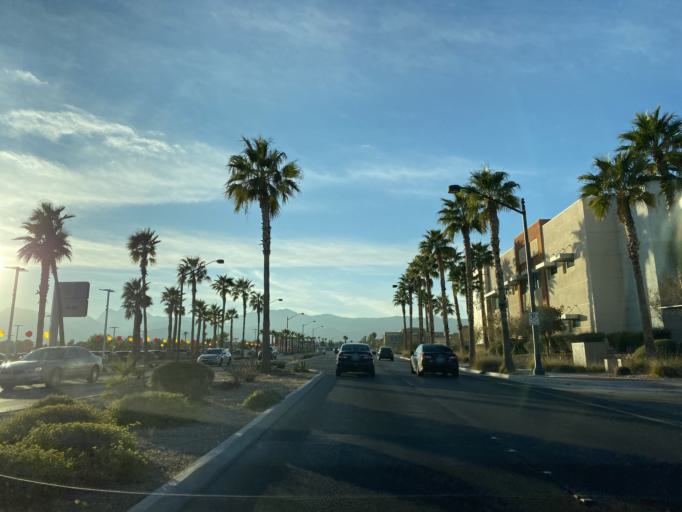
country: US
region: Nevada
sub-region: Clark County
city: Summerlin South
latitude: 36.2774
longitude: -115.2823
